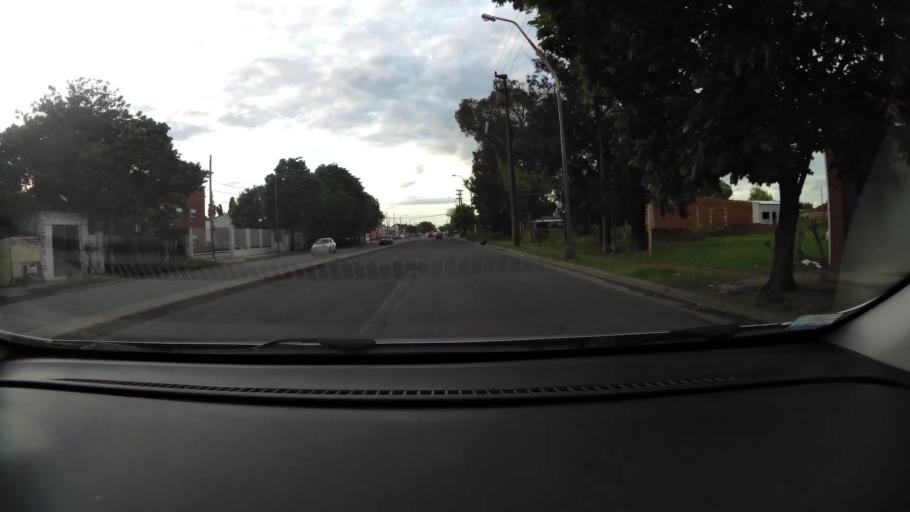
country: AR
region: Buenos Aires
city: San Nicolas de los Arroyos
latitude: -33.3294
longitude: -60.2322
